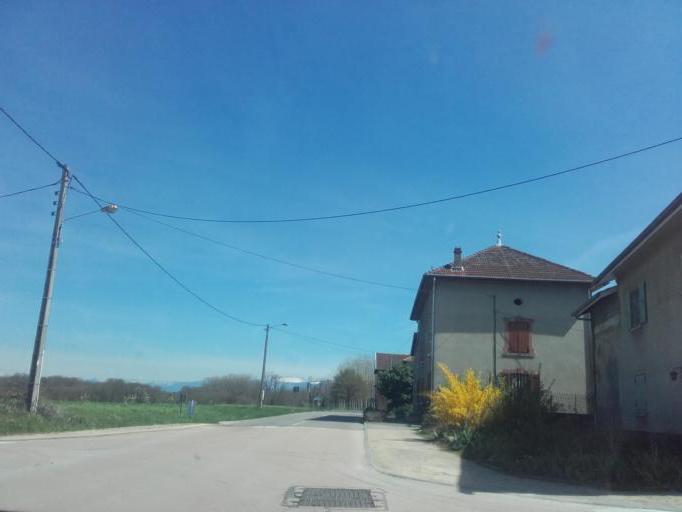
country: FR
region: Rhone-Alpes
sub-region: Departement de l'Isere
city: Saint-Simeon-de-Bressieux
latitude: 45.3298
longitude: 5.2722
